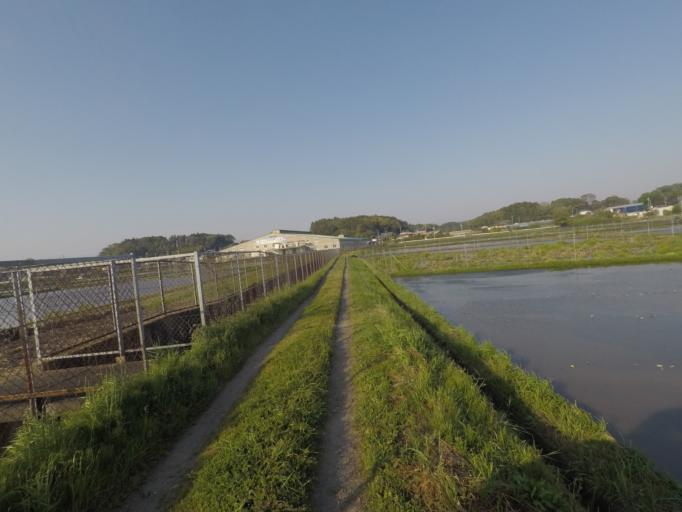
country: JP
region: Ibaraki
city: Ami
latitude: 36.0886
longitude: 140.2385
